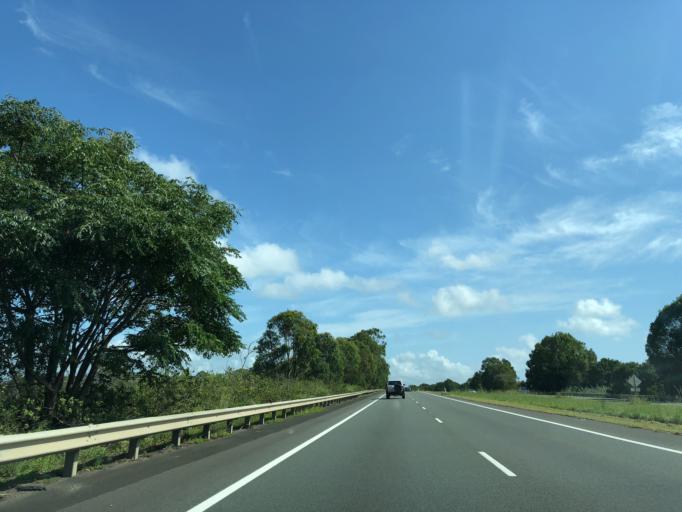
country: AU
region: New South Wales
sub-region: Byron Shire
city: Brunswick Heads
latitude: -28.6074
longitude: 153.5462
